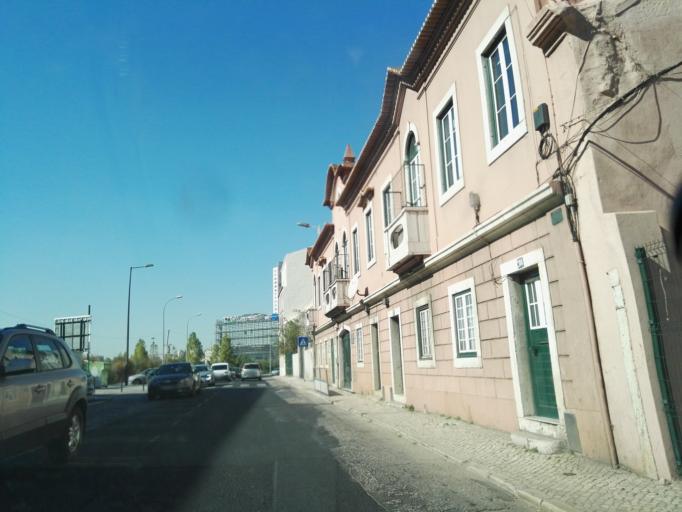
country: PT
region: Lisbon
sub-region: Lisbon
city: Lisbon
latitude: 38.7352
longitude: -9.1653
